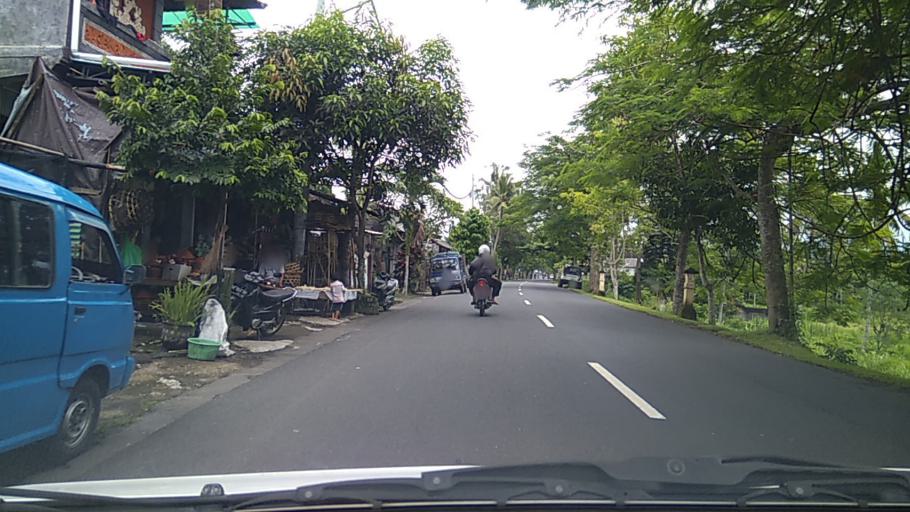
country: ID
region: Bali
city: Banjar Kelodan
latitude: -8.5164
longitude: 115.3457
